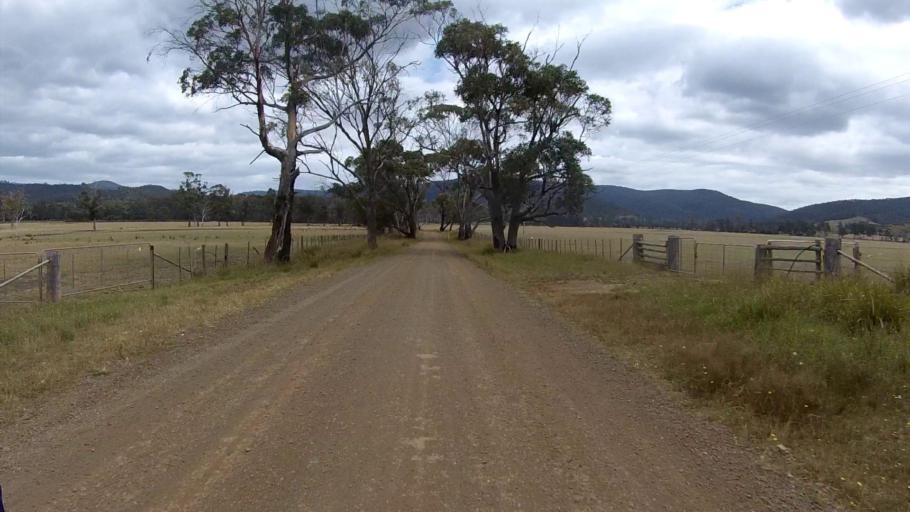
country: AU
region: Tasmania
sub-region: Sorell
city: Sorell
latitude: -42.6357
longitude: 147.9162
